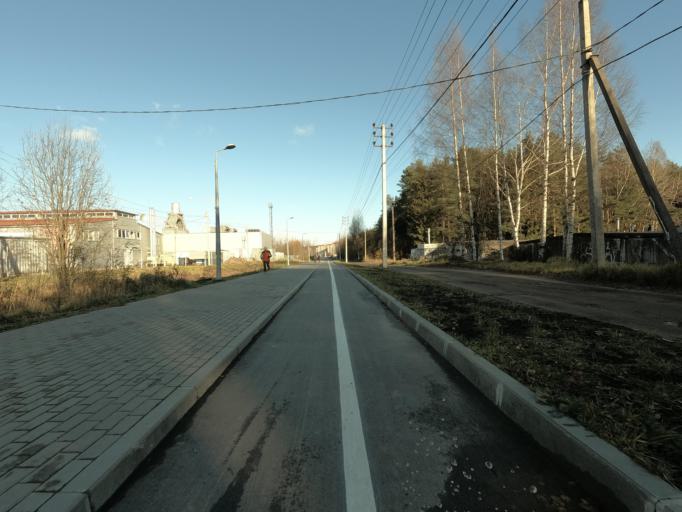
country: RU
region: Leningrad
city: Vsevolozhsk
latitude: 60.0242
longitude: 30.6129
